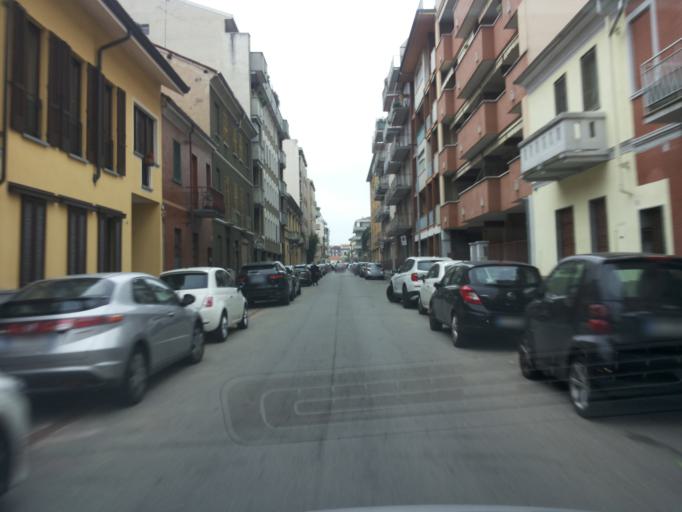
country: IT
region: Piedmont
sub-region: Provincia di Novara
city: Novara
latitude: 45.4408
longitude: 8.6083
